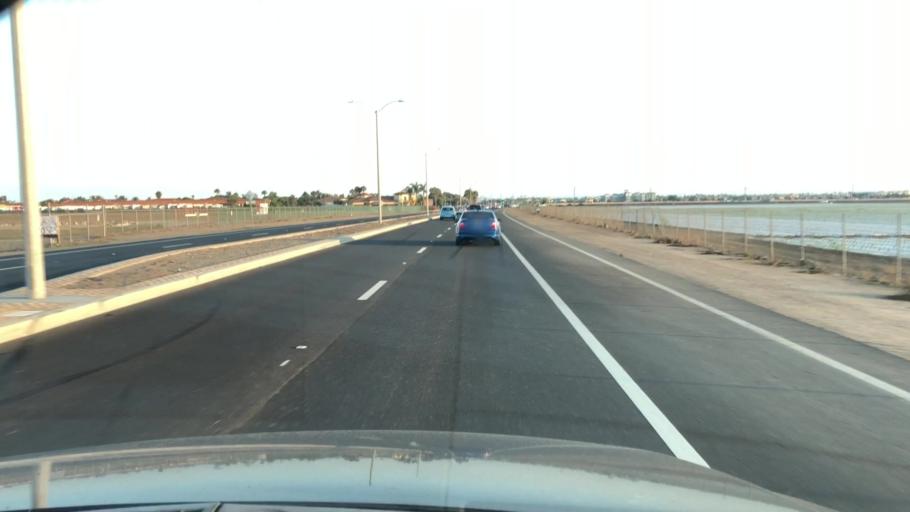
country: US
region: California
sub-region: Ventura County
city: Oxnard Shores
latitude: 34.2024
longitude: -119.2211
